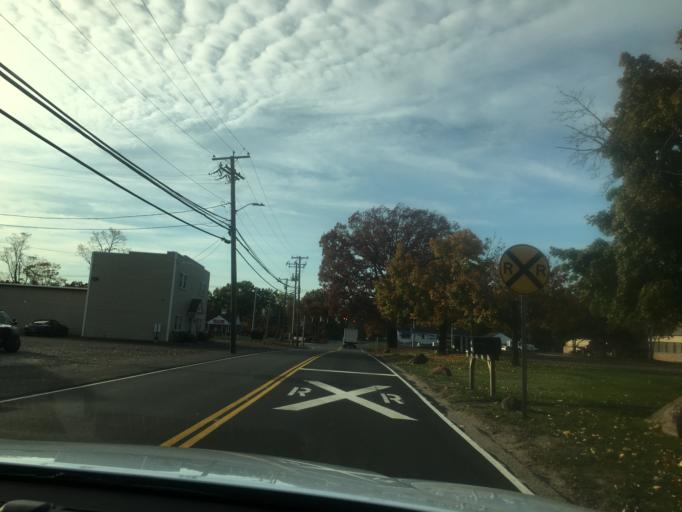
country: US
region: Connecticut
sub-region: Hartford County
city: South Windsor
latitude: 41.8189
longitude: -72.6077
